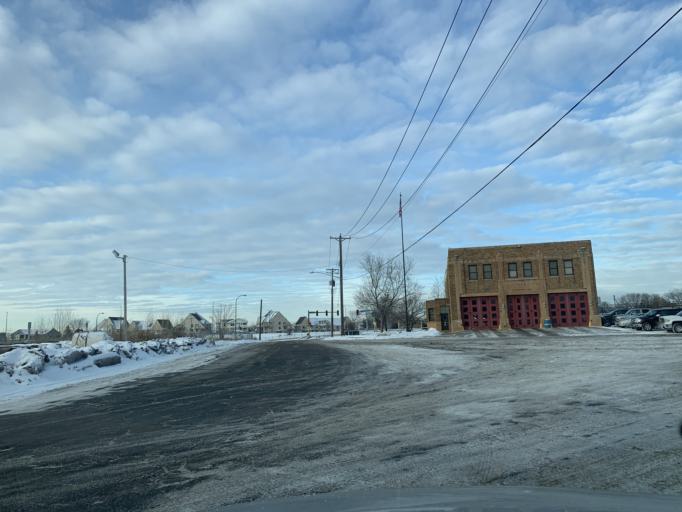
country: US
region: Minnesota
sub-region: Hennepin County
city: Minneapolis
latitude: 44.9894
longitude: -93.2866
